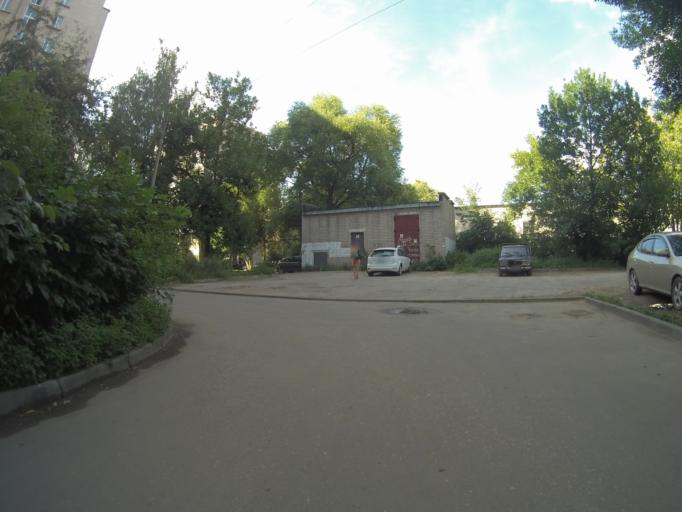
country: RU
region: Vladimir
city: Vladimir
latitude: 56.1324
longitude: 40.3607
